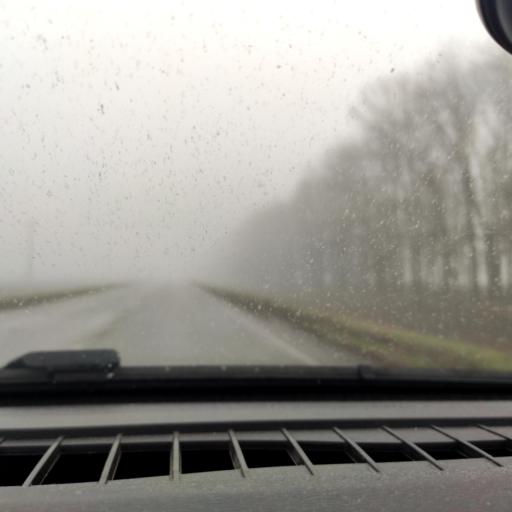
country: RU
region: Belgorod
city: Ilovka
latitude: 50.7465
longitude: 38.7126
